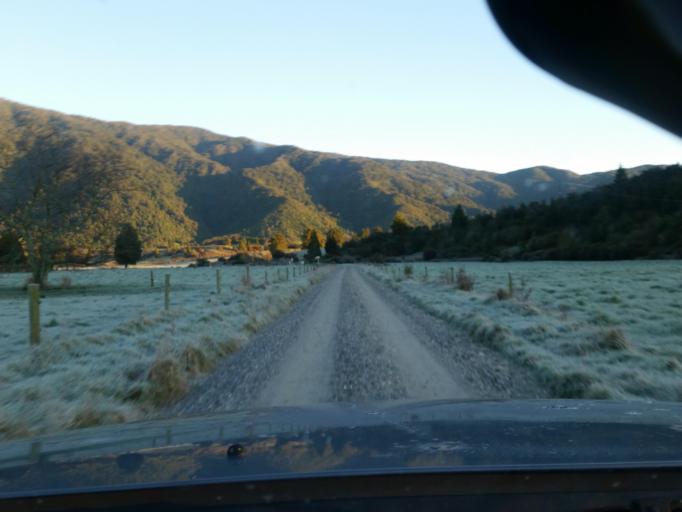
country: NZ
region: Tasman
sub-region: Tasman District
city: Takaka
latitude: -40.7589
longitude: 172.5654
